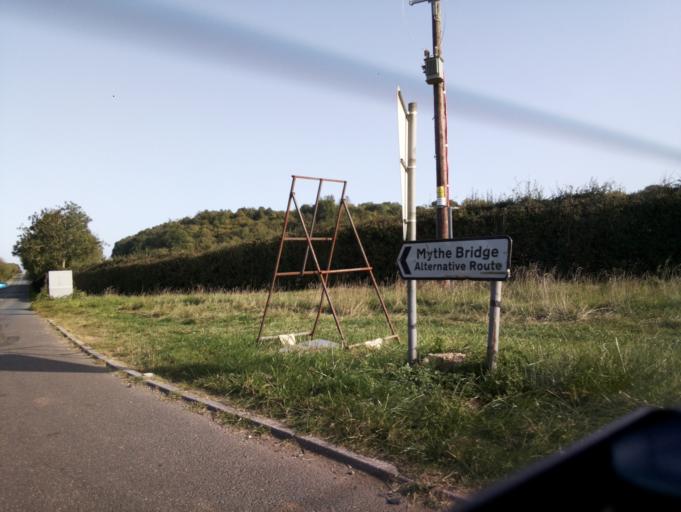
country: GB
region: England
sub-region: Gloucestershire
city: Gloucester
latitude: 51.9626
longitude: -2.2736
